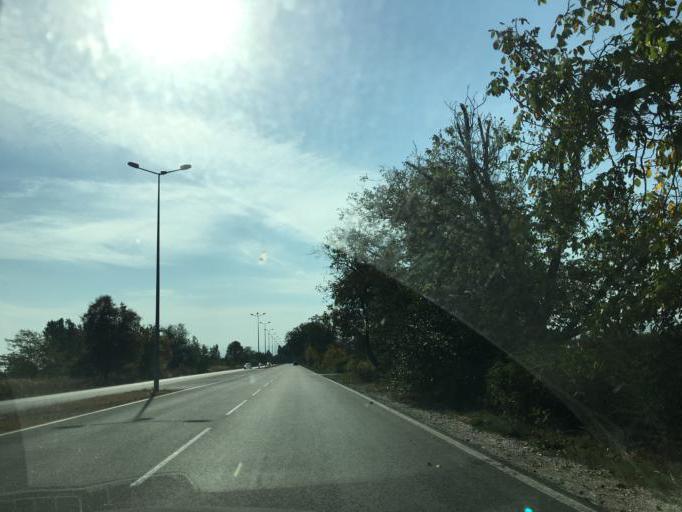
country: BG
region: Pazardzhik
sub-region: Obshtina Pazardzhik
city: Pazardzhik
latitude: 42.2204
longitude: 24.3125
